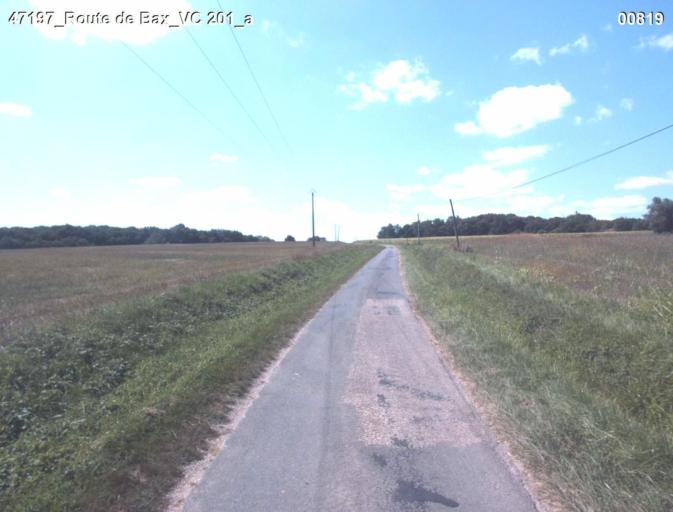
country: FR
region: Aquitaine
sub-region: Departement du Lot-et-Garonne
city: Laplume
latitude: 44.0702
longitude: 0.4843
